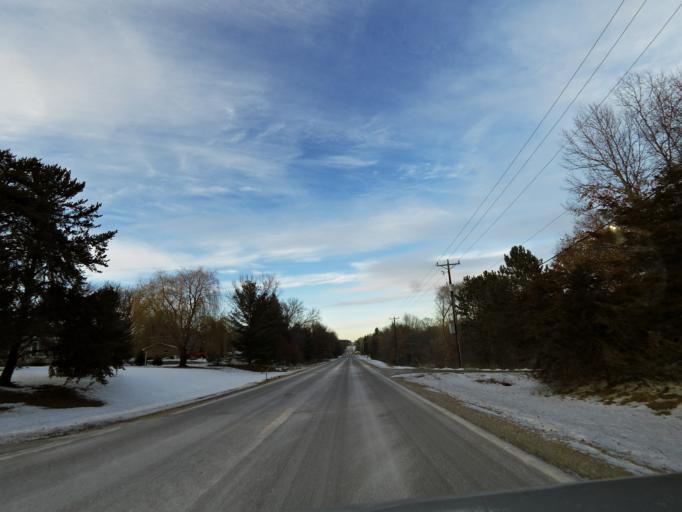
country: US
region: Minnesota
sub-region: Washington County
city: Afton
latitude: 44.9020
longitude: -92.8429
